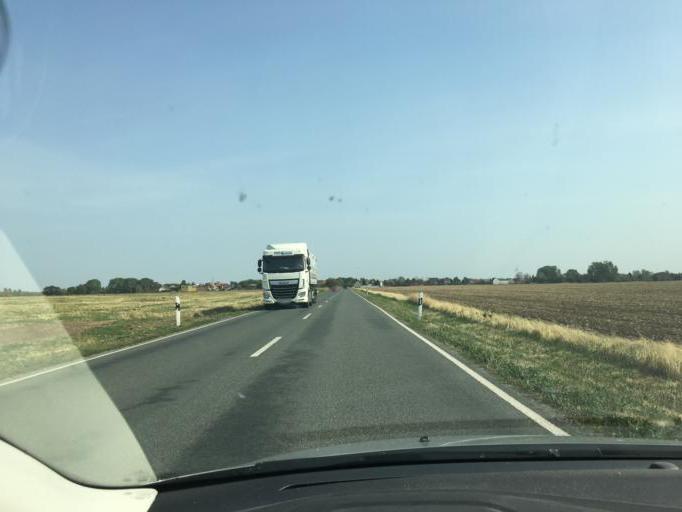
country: DE
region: Saxony-Anhalt
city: Plotzky
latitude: 51.9983
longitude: 11.8223
